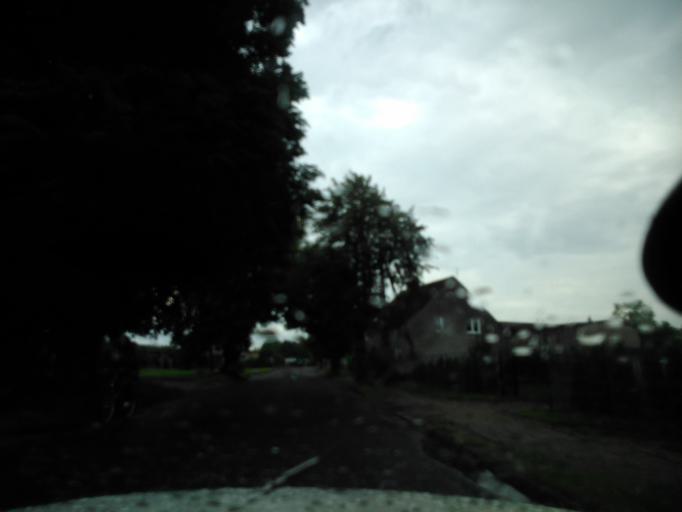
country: PL
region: Pomeranian Voivodeship
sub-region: Powiat slupski
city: Smoldzino
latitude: 54.6639
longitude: 17.2157
